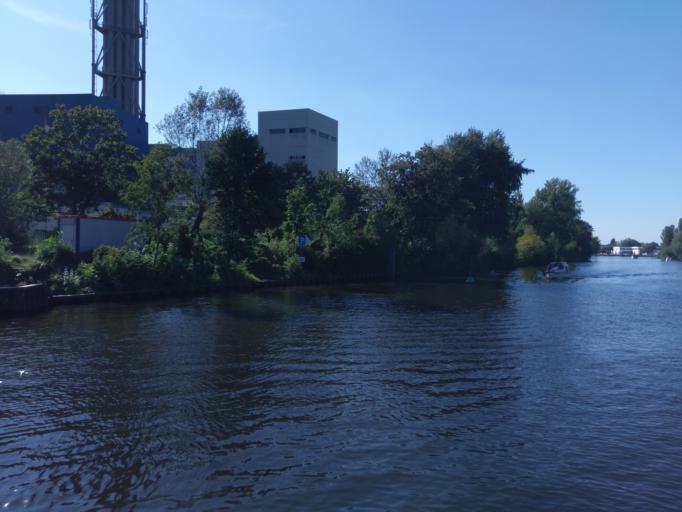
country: DE
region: Berlin
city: Haselhorst
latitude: 52.5314
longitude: 13.2413
